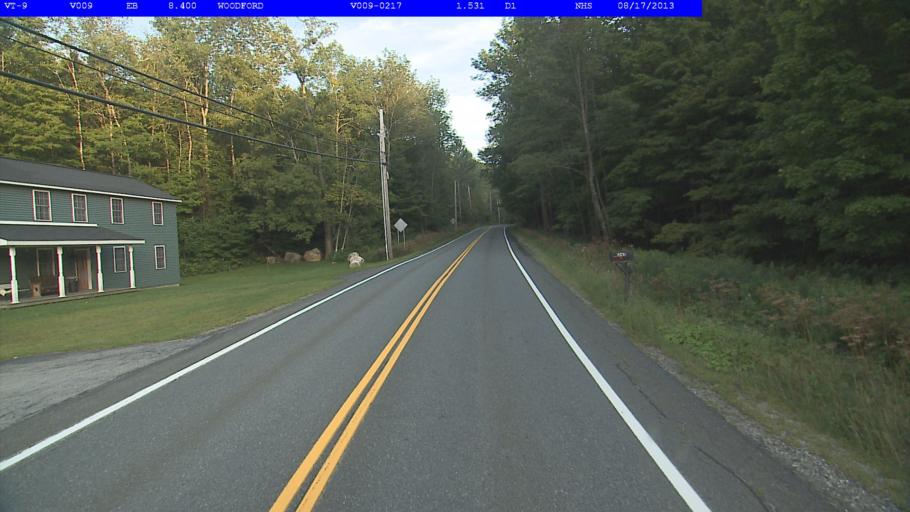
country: US
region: Vermont
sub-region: Bennington County
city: Bennington
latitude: 42.8958
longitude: -73.1276
